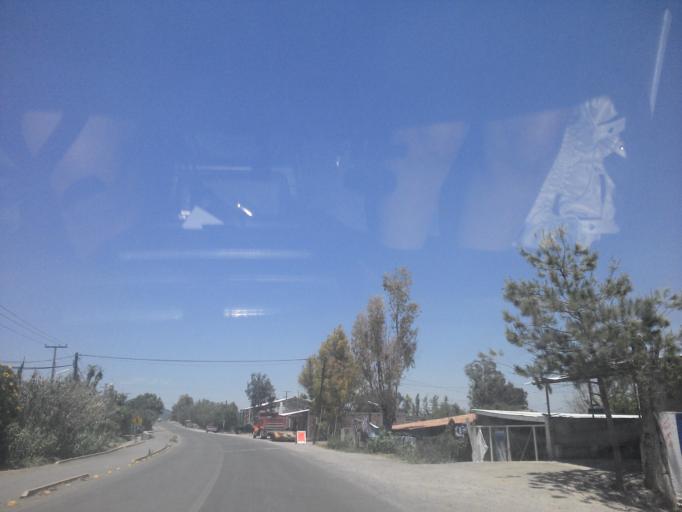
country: MX
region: Guanajuato
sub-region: San Francisco del Rincon
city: San Ignacio de Hidalgo
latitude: 20.9007
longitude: -101.9186
